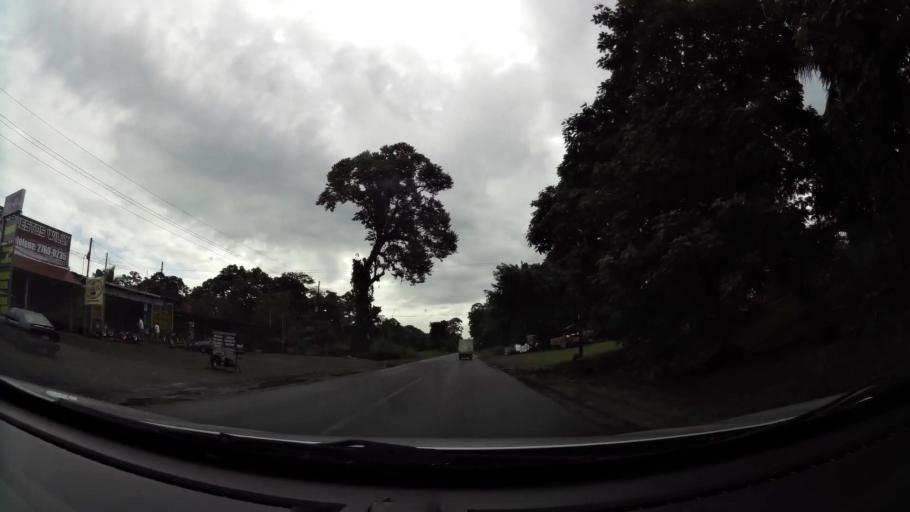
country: CR
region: Limon
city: Pocora
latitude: 10.1446
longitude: -83.5750
